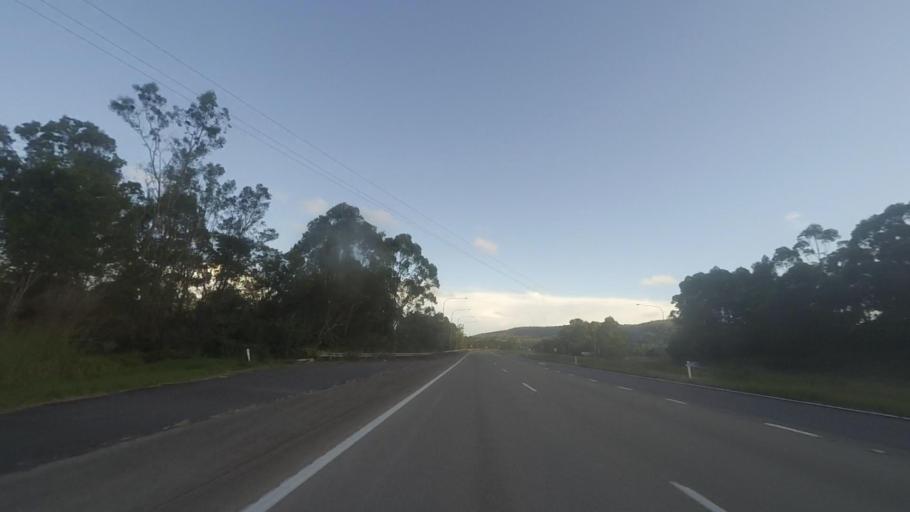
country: AU
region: New South Wales
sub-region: Great Lakes
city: Nabiac
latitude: -32.2599
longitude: 152.3265
